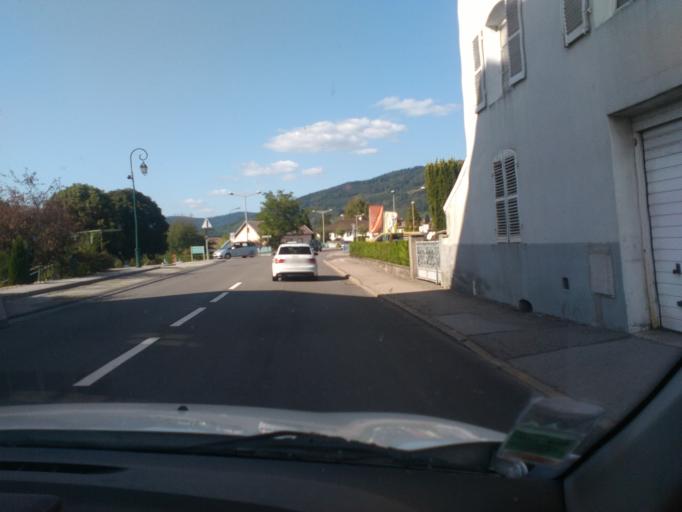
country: FR
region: Lorraine
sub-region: Departement des Vosges
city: Vagney
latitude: 48.0089
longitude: 6.7167
